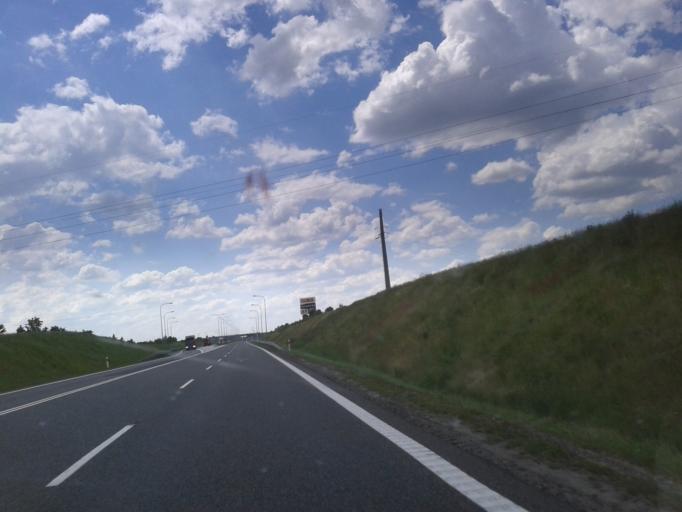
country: PL
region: Pomeranian Voivodeship
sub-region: Powiat chojnicki
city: Chojnice
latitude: 53.6956
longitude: 17.6264
